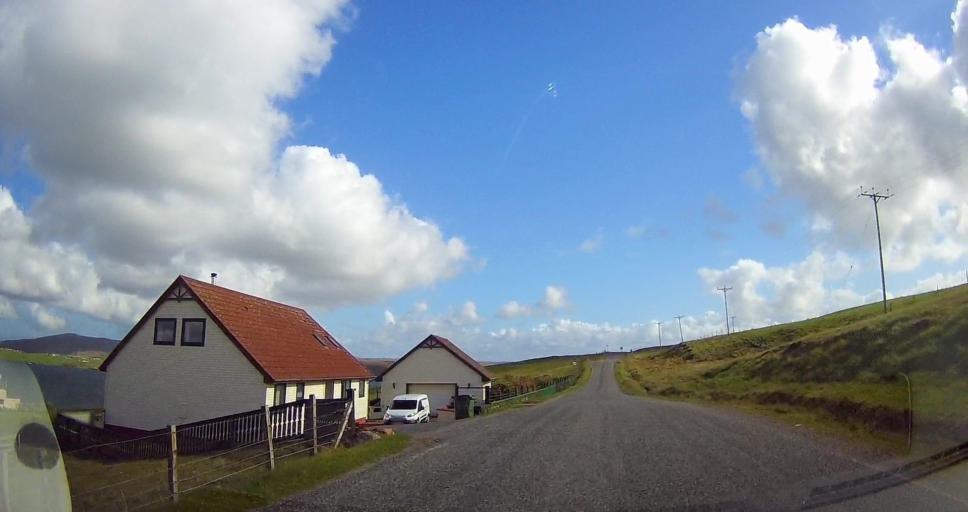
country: GB
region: Scotland
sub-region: Shetland Islands
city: Lerwick
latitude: 60.3833
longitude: -1.3790
